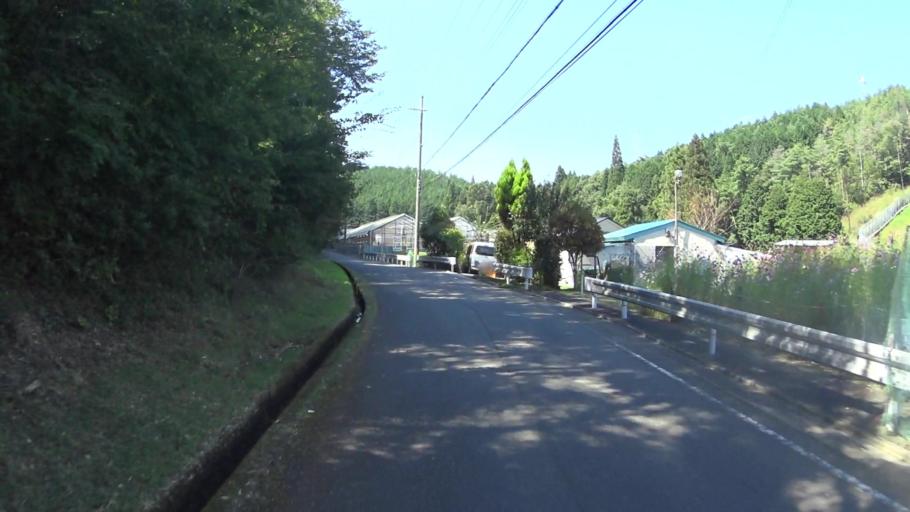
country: JP
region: Kyoto
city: Kameoka
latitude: 34.9674
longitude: 135.6176
